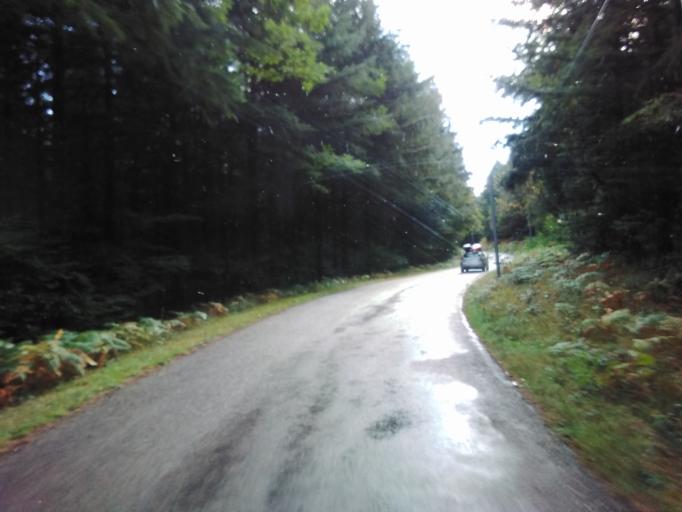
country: FR
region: Bourgogne
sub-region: Departement de la Nievre
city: Lormes
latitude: 47.2901
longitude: 3.8438
